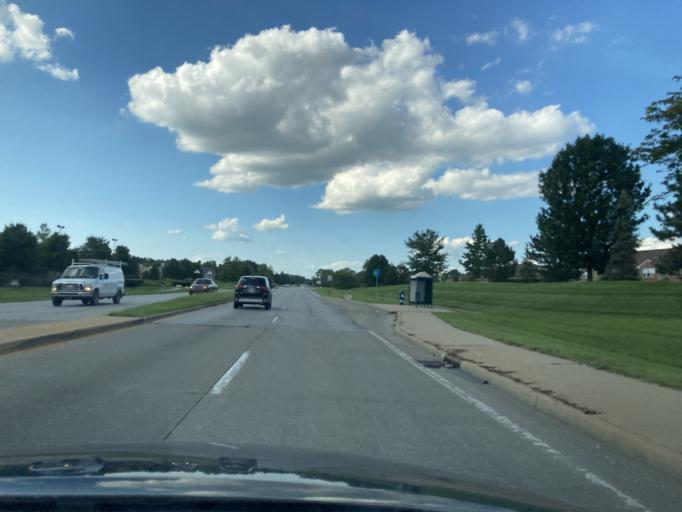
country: US
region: Indiana
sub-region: Marion County
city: Speedway
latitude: 39.8678
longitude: -86.2442
